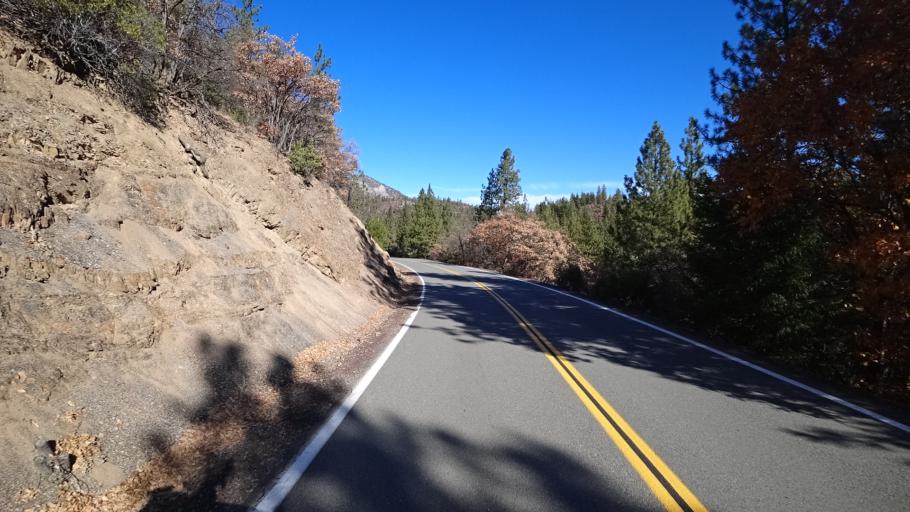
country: US
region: California
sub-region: Siskiyou County
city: Weed
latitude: 41.4530
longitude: -122.6370
